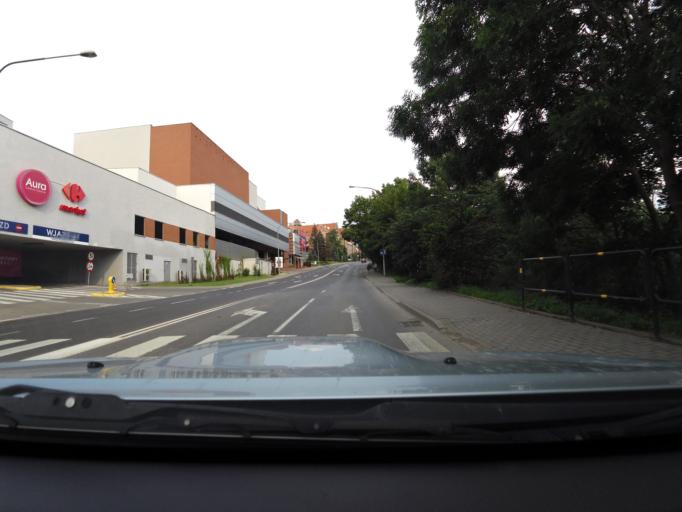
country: PL
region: Warmian-Masurian Voivodeship
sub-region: Powiat olsztynski
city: Olsztyn
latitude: 53.7766
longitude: 20.4825
